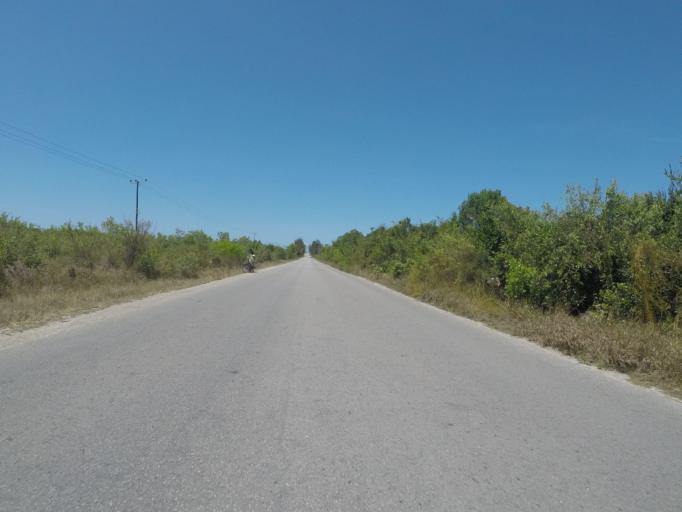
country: TZ
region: Zanzibar Central/South
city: Nganane
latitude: -6.2697
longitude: 39.5115
